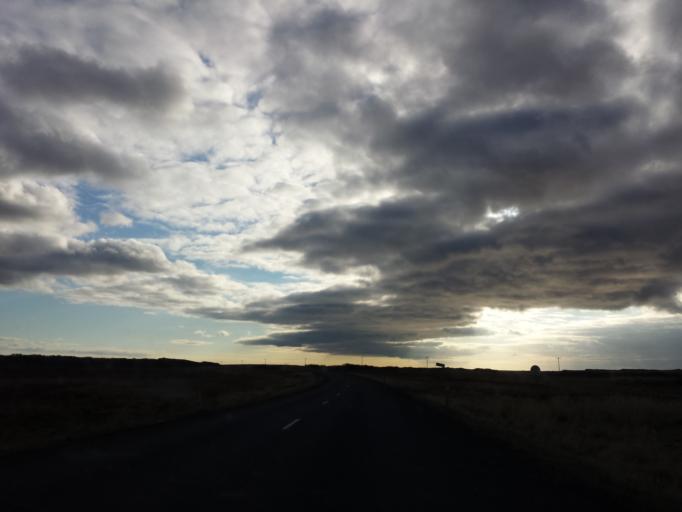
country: IS
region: West
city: Borgarnes
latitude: 64.6433
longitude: -22.0663
